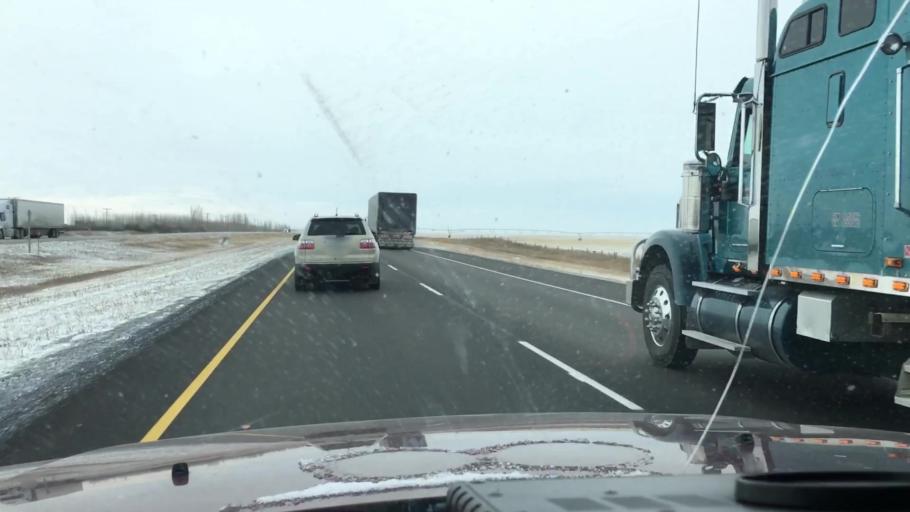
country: CA
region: Saskatchewan
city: Saskatoon
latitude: 51.7762
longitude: -106.4764
